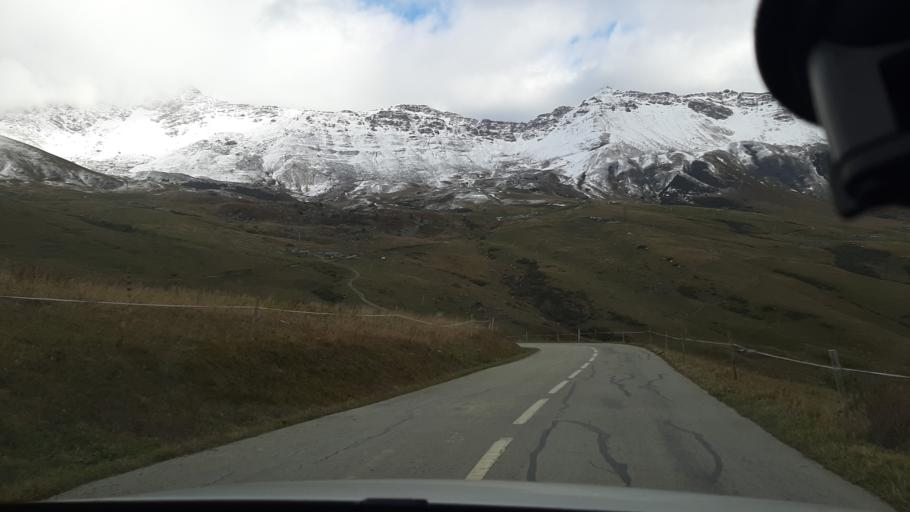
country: FR
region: Rhone-Alpes
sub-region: Departement de la Savoie
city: La Chambre
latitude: 45.4263
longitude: 6.3700
